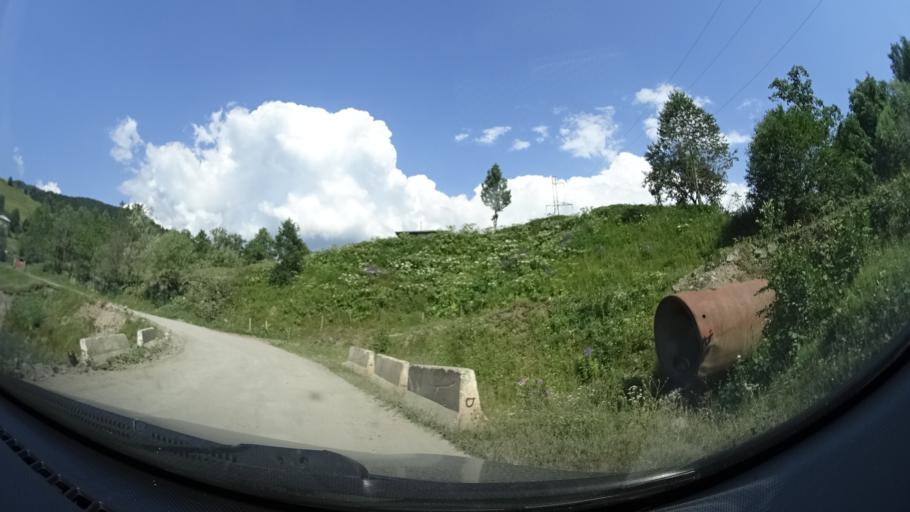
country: GE
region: Ajaria
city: Dioknisi
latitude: 41.6429
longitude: 42.4649
